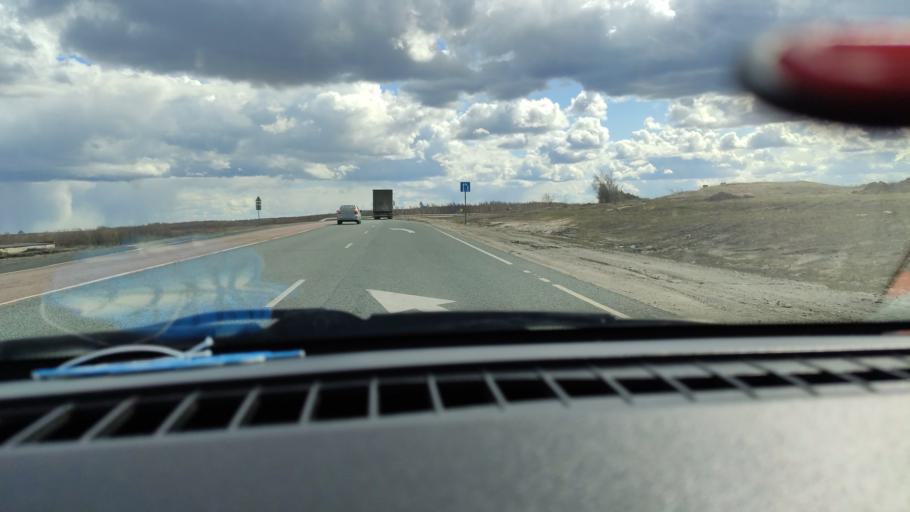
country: RU
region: Samara
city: Syzran'
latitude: 52.9534
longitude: 48.3070
